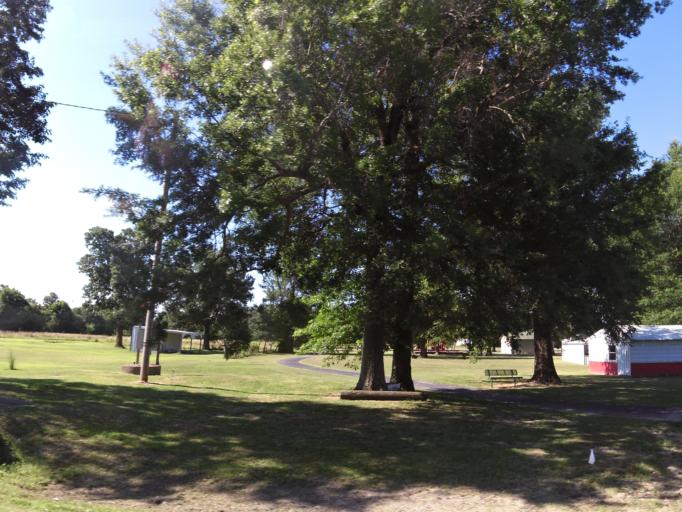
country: US
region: Arkansas
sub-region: Clay County
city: Corning
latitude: 36.4345
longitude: -90.3926
